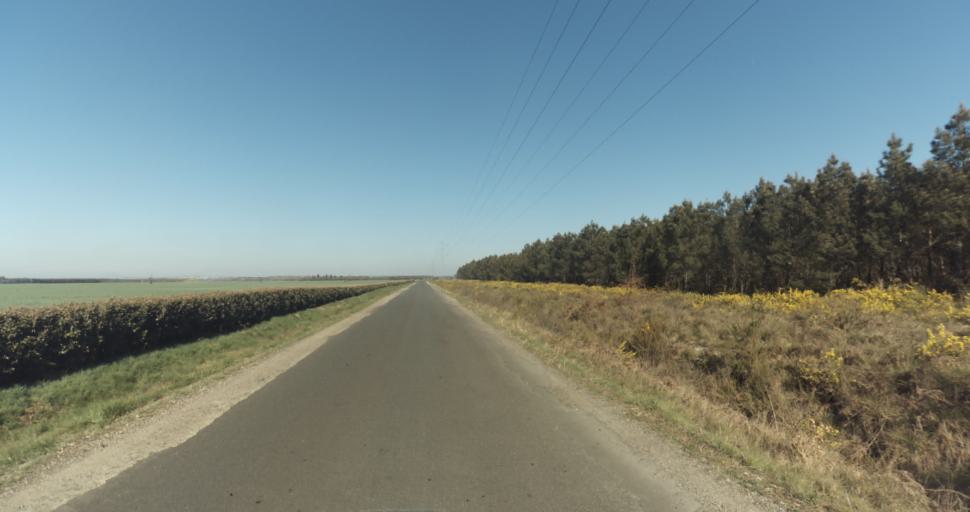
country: FR
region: Aquitaine
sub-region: Departement de la Gironde
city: Marcheprime
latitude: 44.7434
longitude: -0.8289
